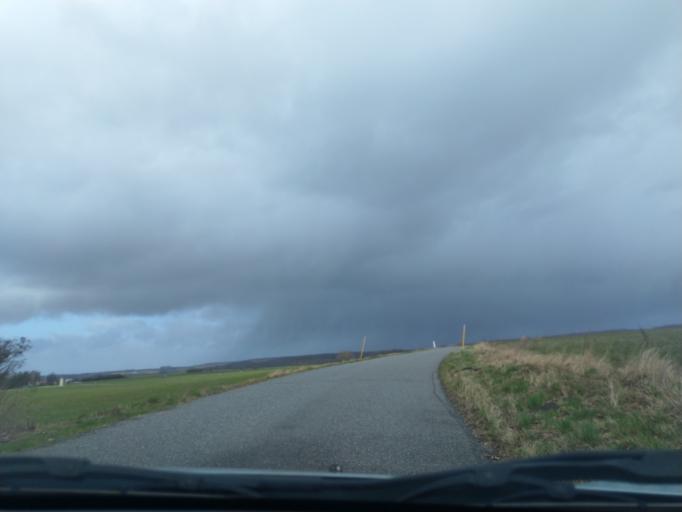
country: DK
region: Zealand
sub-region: Naestved Kommune
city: Fuglebjerg
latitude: 55.3468
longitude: 11.5834
